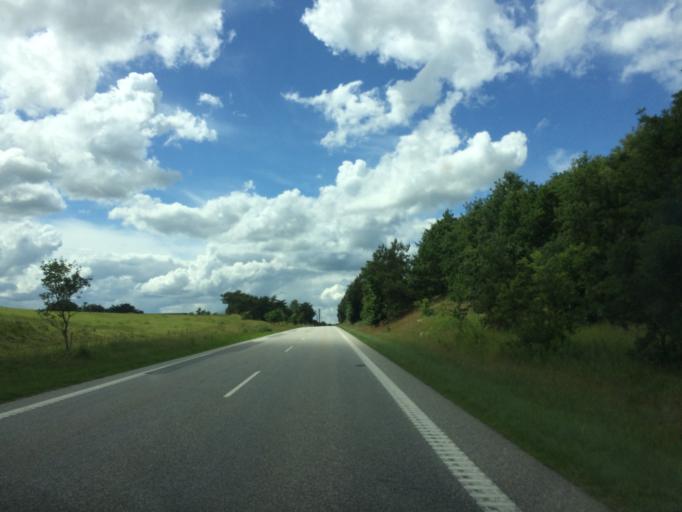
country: DK
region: North Denmark
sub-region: Vesthimmerland Kommune
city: Alestrup
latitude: 56.6218
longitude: 9.5348
